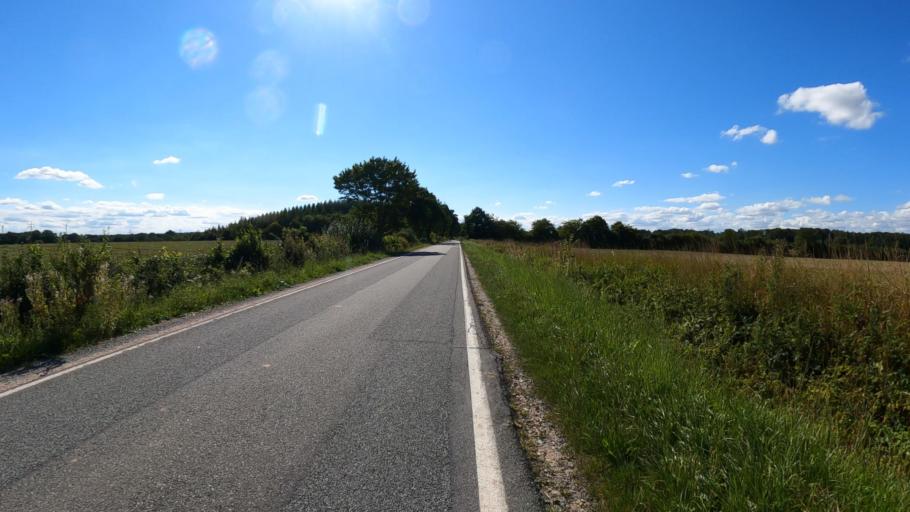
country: DE
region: Schleswig-Holstein
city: Grinau
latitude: 53.7963
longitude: 10.5462
